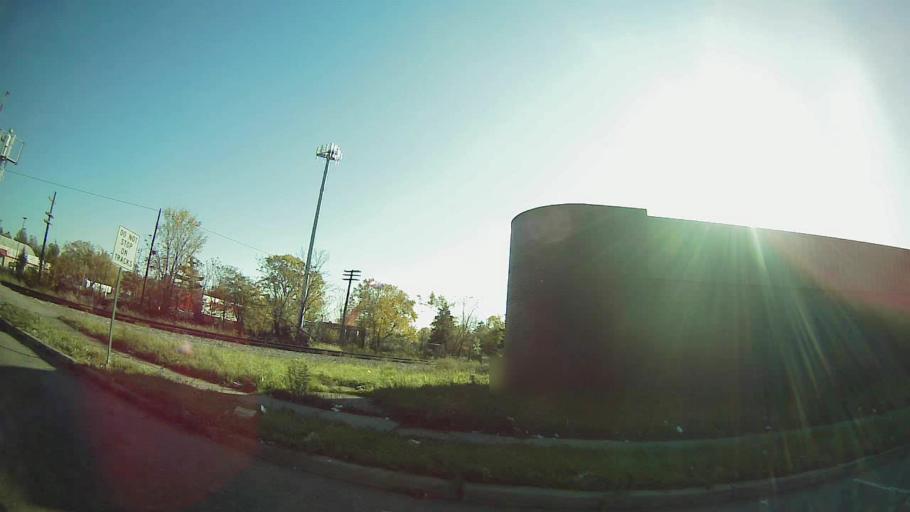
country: US
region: Michigan
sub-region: Macomb County
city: Warren
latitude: 42.4340
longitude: -83.0168
